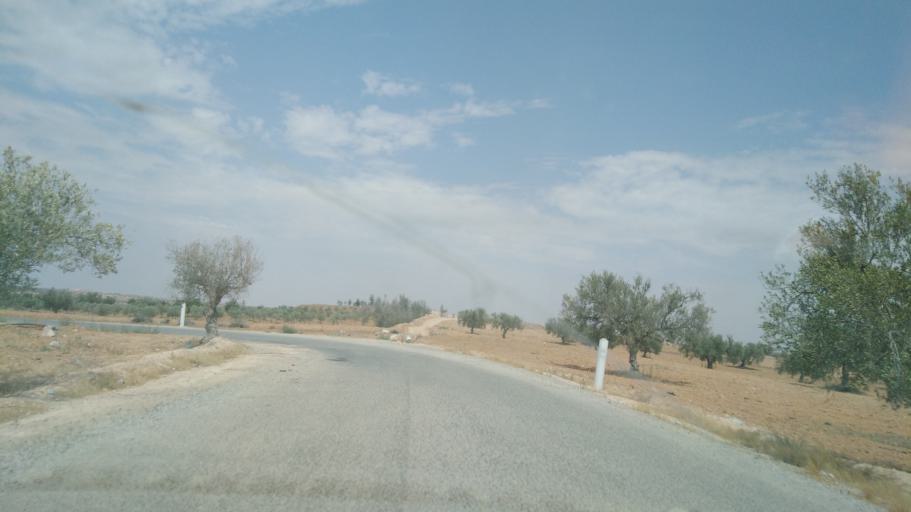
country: TN
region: Safaqis
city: Sfax
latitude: 34.7483
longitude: 10.5609
